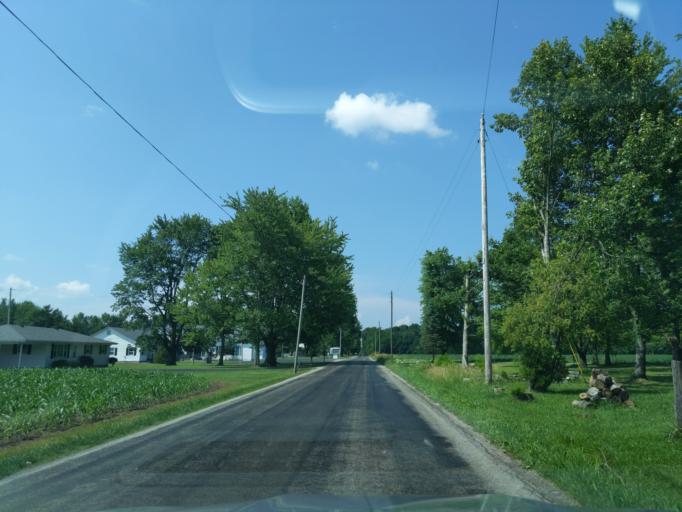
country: US
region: Indiana
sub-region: Ripley County
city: Osgood
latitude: 39.0907
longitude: -85.3465
